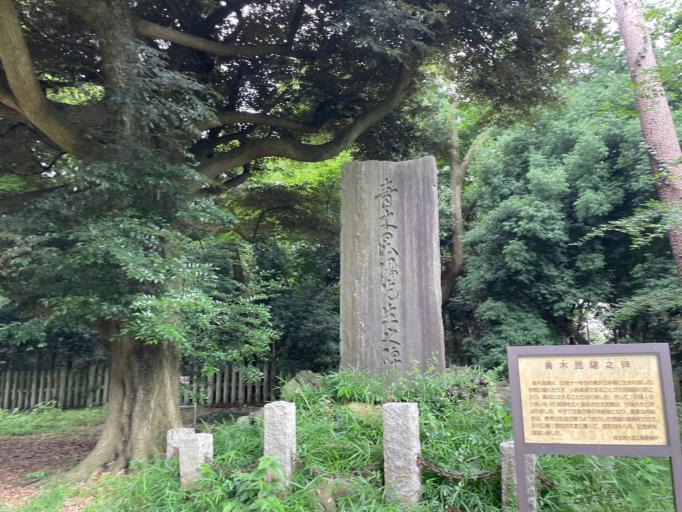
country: JP
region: Saitama
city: Saitama
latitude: 35.9181
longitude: 139.6303
